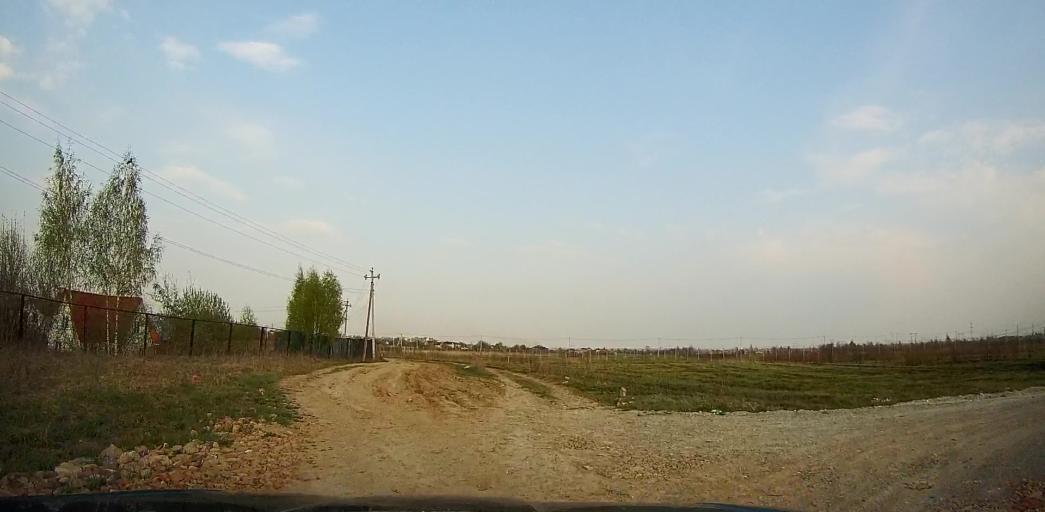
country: RU
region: Moskovskaya
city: Andreyevskoye
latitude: 55.5501
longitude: 37.9444
